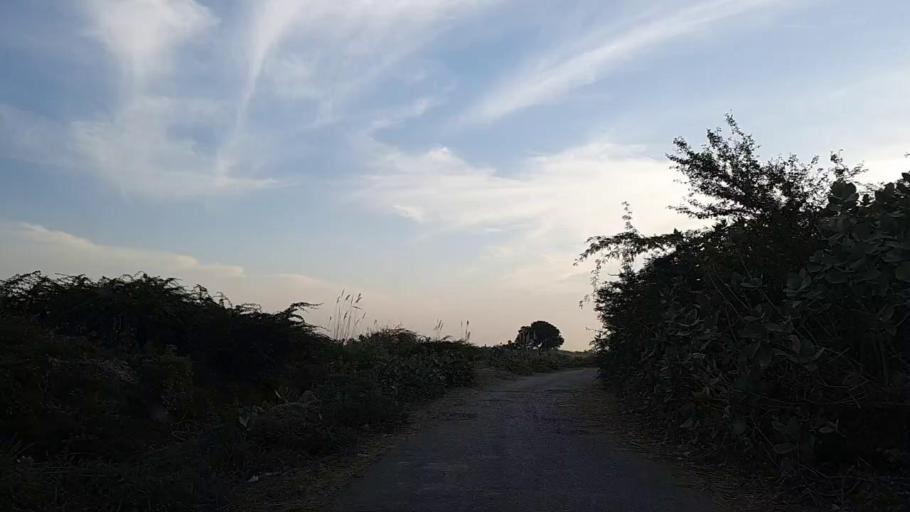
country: PK
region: Sindh
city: Mirpur Batoro
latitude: 24.6411
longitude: 68.1408
